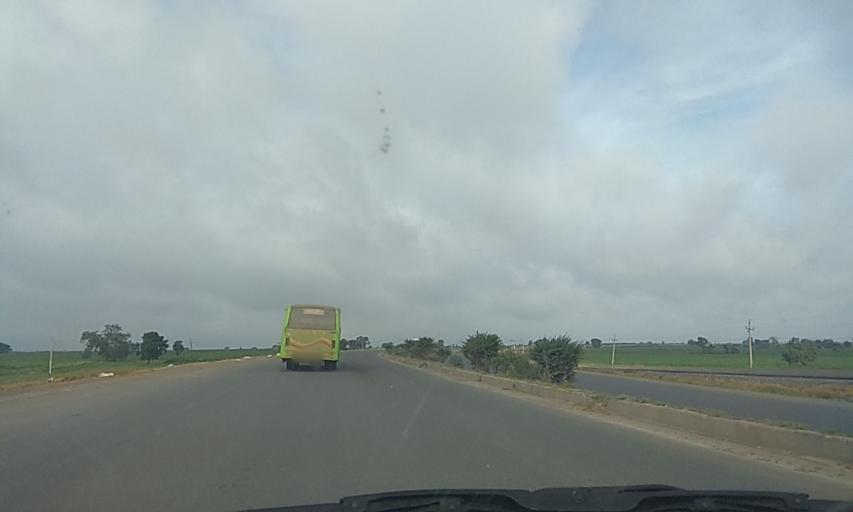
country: IN
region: Karnataka
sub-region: Haveri
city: Haveri
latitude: 14.8419
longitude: 75.3442
